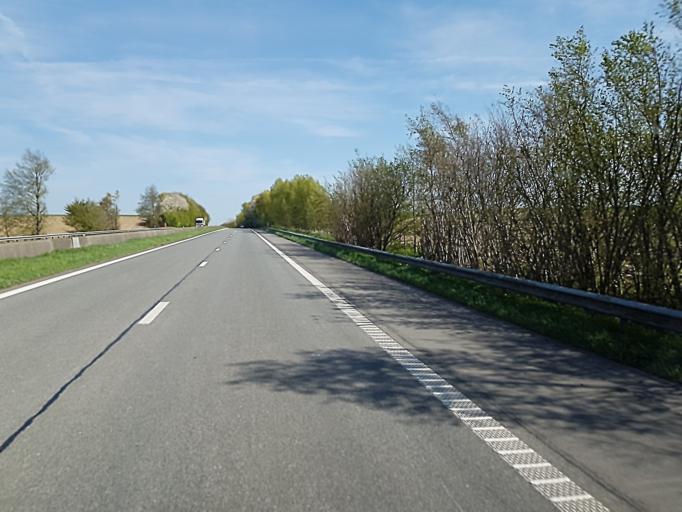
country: BE
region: Wallonia
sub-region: Province du Hainaut
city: Lessines
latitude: 50.6728
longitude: 3.8449
